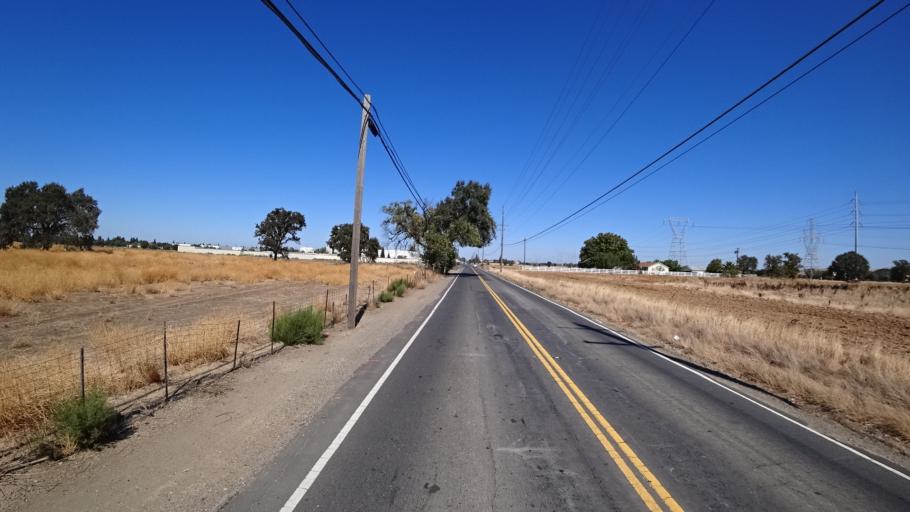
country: US
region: California
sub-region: Sacramento County
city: Elk Grove
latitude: 38.3931
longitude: -121.3530
